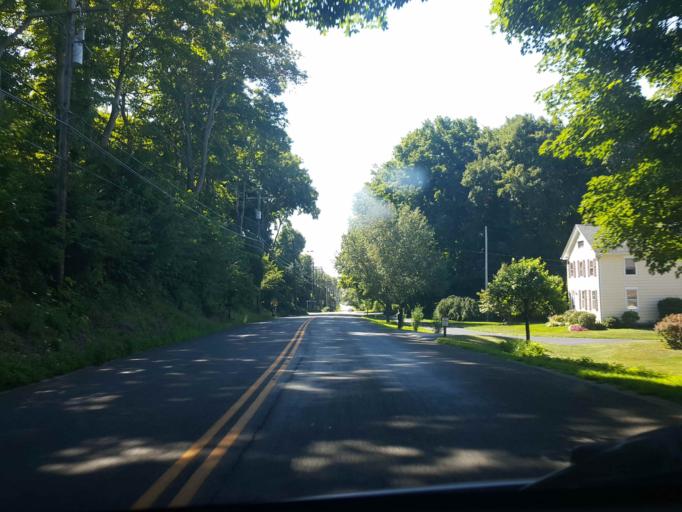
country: US
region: Connecticut
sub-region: New Haven County
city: Guilford
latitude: 41.3029
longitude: -72.6999
